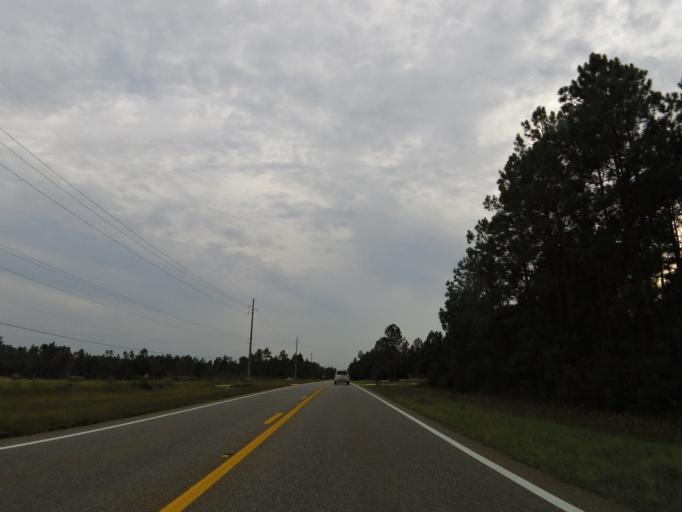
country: US
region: Alabama
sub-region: Escambia County
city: Atmore
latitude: 30.9829
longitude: -87.6290
